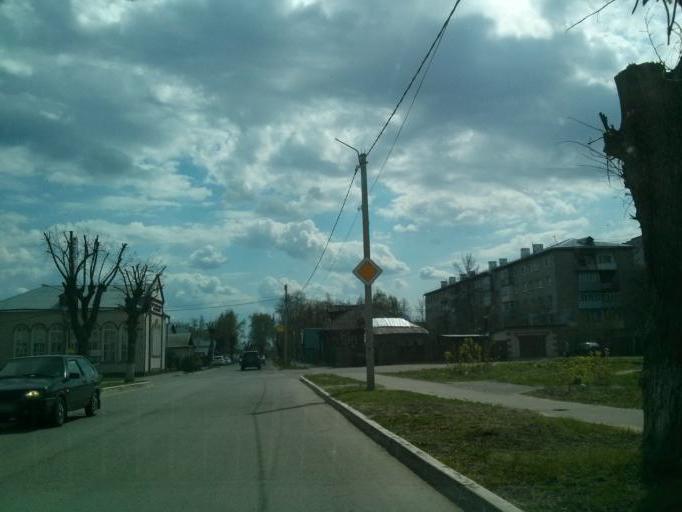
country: RU
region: Vladimir
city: Murom
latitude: 55.5680
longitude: 42.0653
